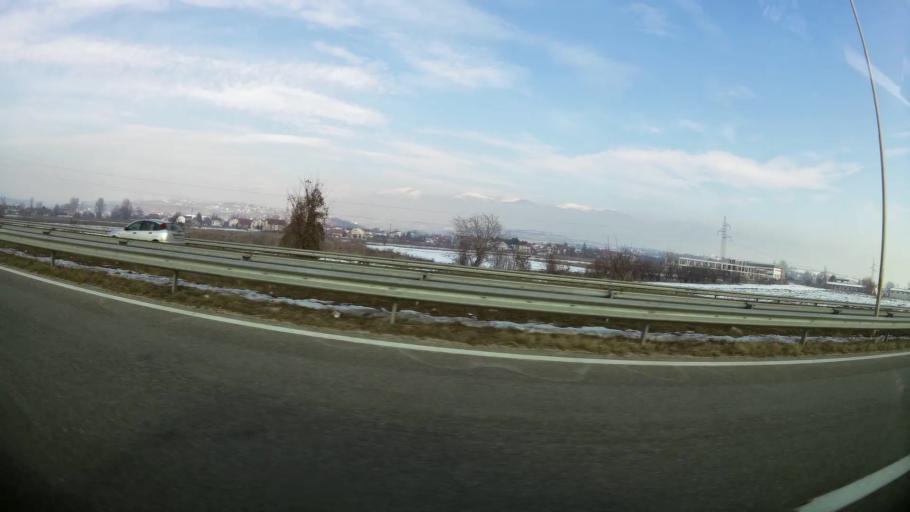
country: MK
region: Butel
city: Butel
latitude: 42.0440
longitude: 21.4448
